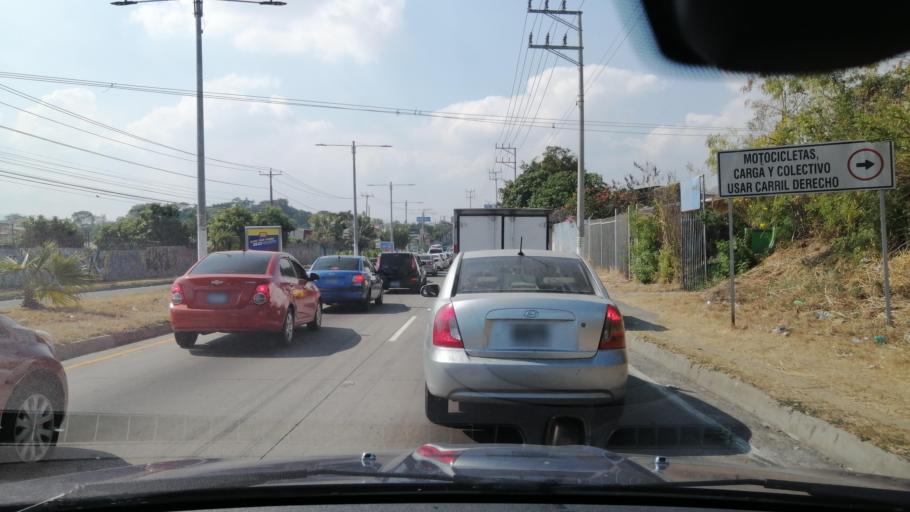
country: SV
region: San Salvador
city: Mejicanos
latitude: 13.7410
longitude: -89.2174
